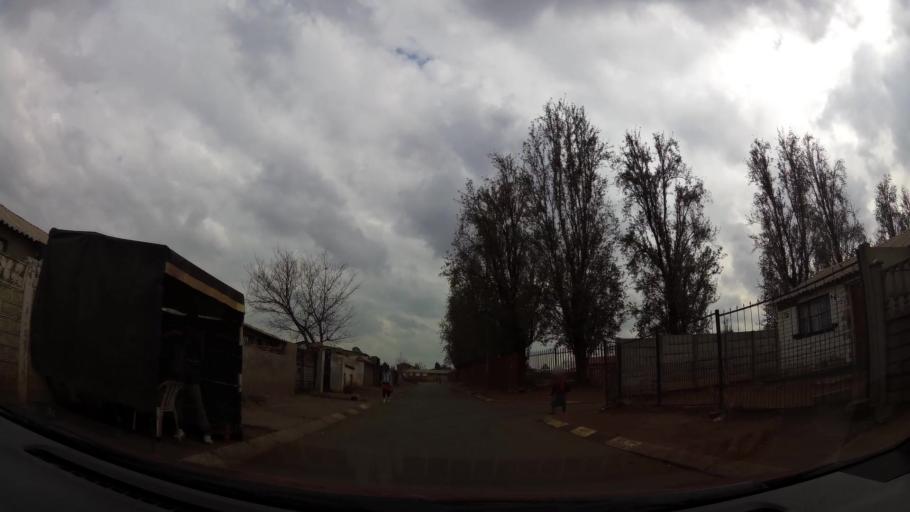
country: ZA
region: Gauteng
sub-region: City of Johannesburg Metropolitan Municipality
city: Soweto
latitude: -26.2576
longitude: 27.8343
